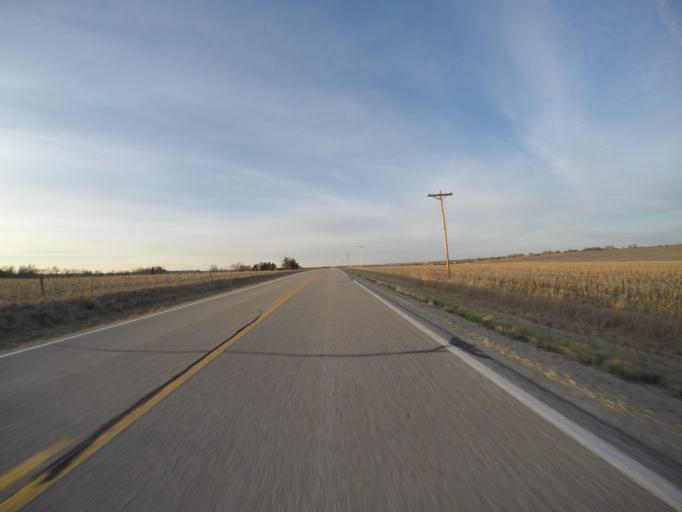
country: US
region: Kansas
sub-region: Clay County
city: Clay Center
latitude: 39.4085
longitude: -96.8489
